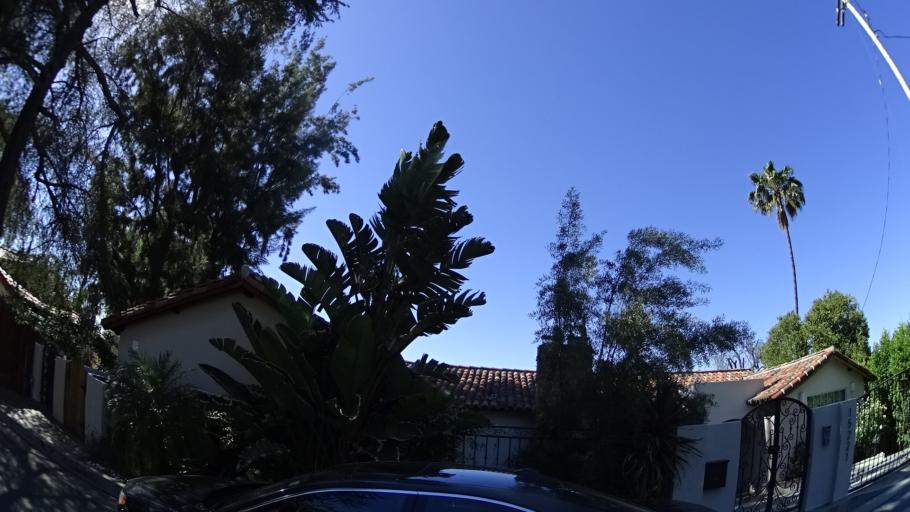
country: US
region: California
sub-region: Los Angeles County
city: Sherman Oaks
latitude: 34.1478
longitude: -118.4649
